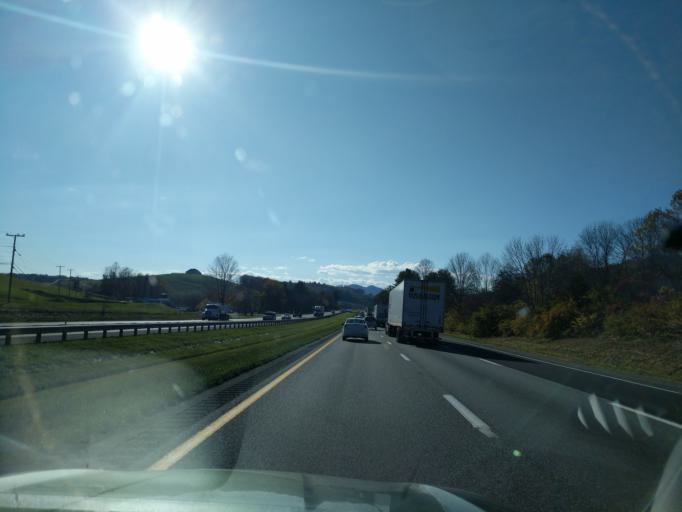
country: US
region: Virginia
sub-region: Pulaski County
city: Pulaski
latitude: 36.9955
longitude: -80.7874
